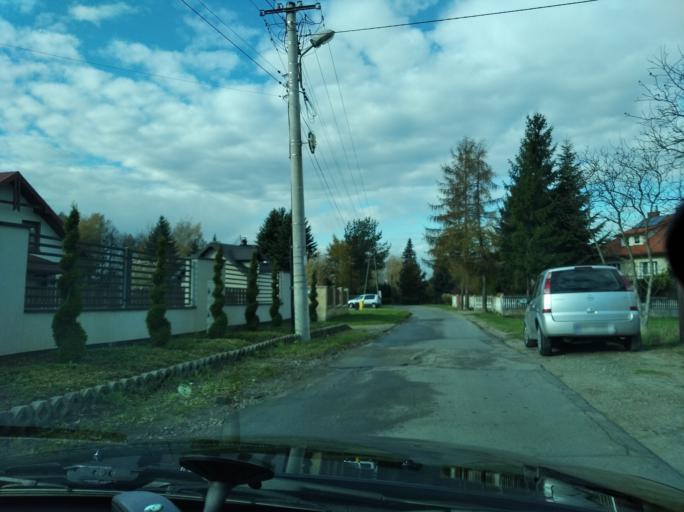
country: PL
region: Subcarpathian Voivodeship
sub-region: Powiat debicki
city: Debica
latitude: 50.0403
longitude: 21.4461
